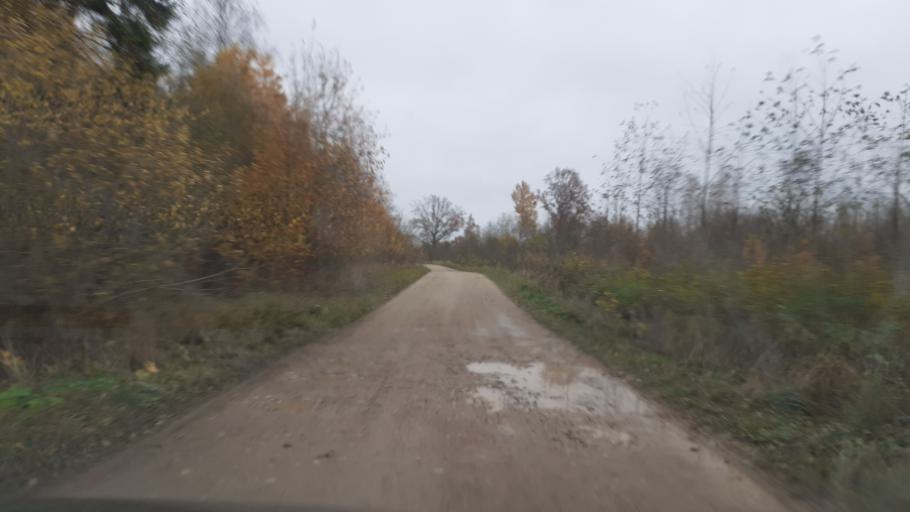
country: LV
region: Saldus Rajons
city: Saldus
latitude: 56.8609
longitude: 22.3343
